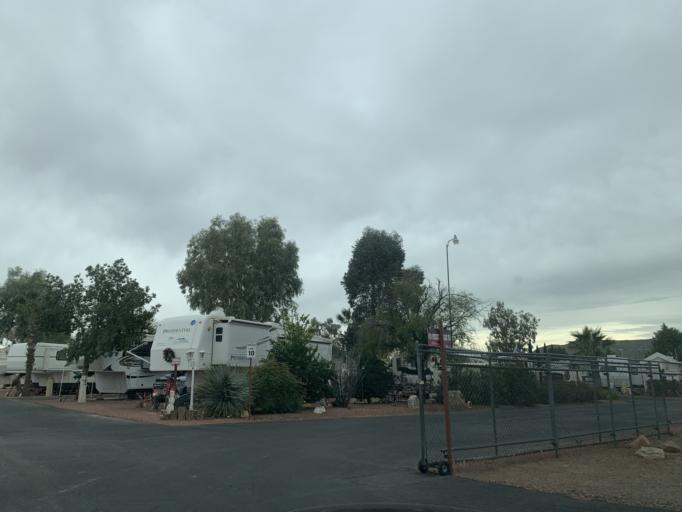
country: US
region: Arizona
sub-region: Pinal County
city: Arizona City
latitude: 32.8154
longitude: -111.6739
